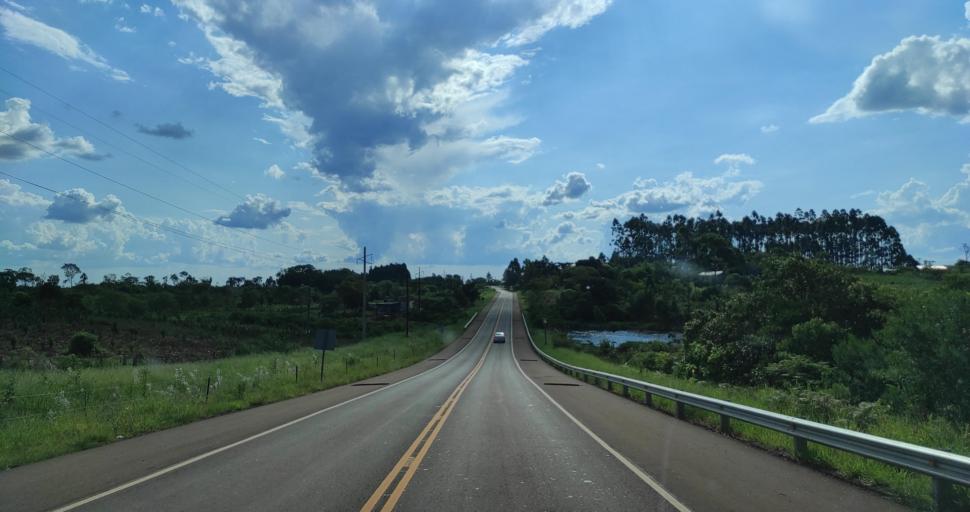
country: AR
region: Misiones
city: Bernardo de Irigoyen
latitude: -26.2952
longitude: -53.7821
